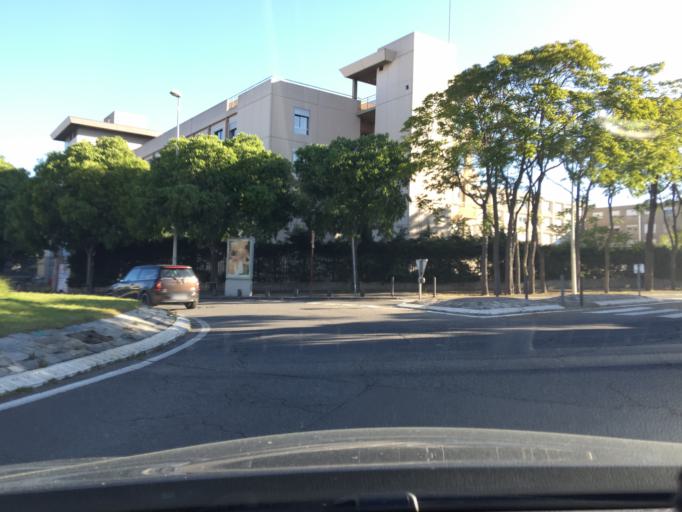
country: FR
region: Provence-Alpes-Cote d'Azur
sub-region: Departement des Bouches-du-Rhone
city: Marseille 09
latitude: 43.2579
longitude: 5.4102
